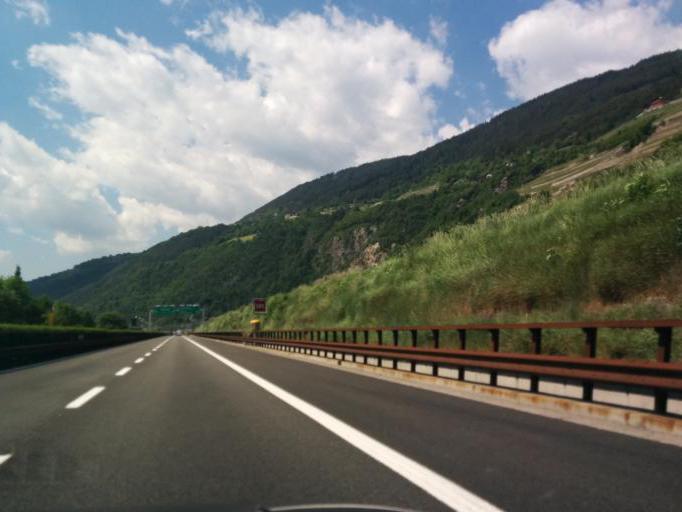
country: IT
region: Trentino-Alto Adige
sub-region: Bolzano
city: Bressanone
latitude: 46.6881
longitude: 11.6340
